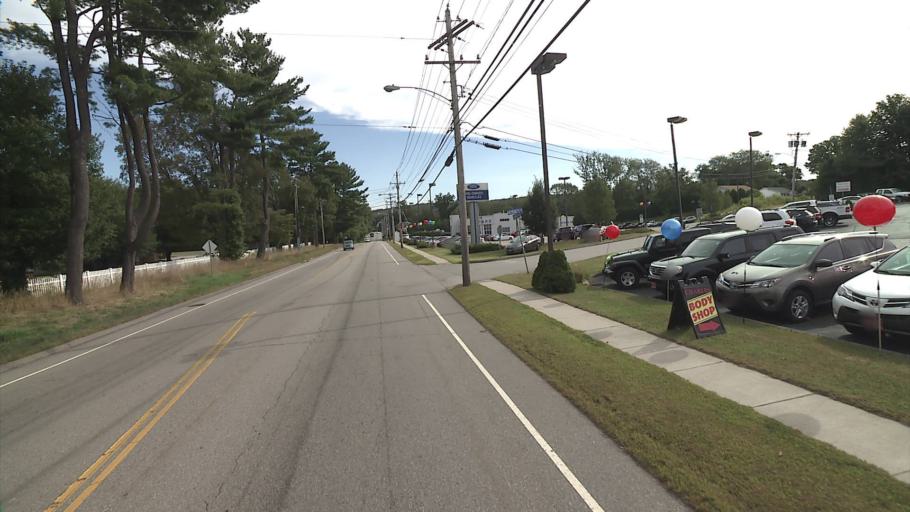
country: US
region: Connecticut
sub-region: New London County
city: Norwich
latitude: 41.5042
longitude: -72.0912
